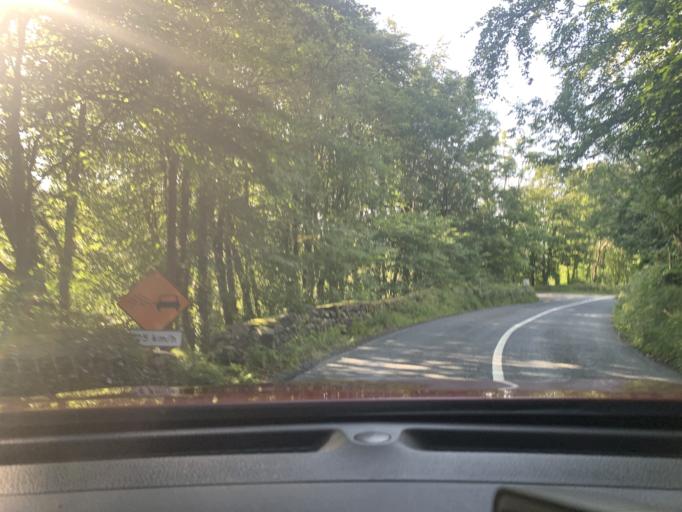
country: IE
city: Ballisodare
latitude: 54.1949
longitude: -8.5842
